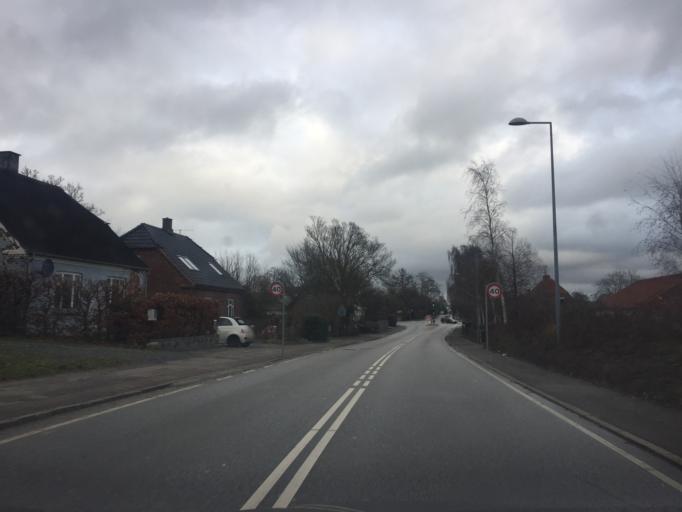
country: DK
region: Zealand
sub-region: Holbaek Kommune
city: Tollose
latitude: 55.6144
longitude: 11.7602
